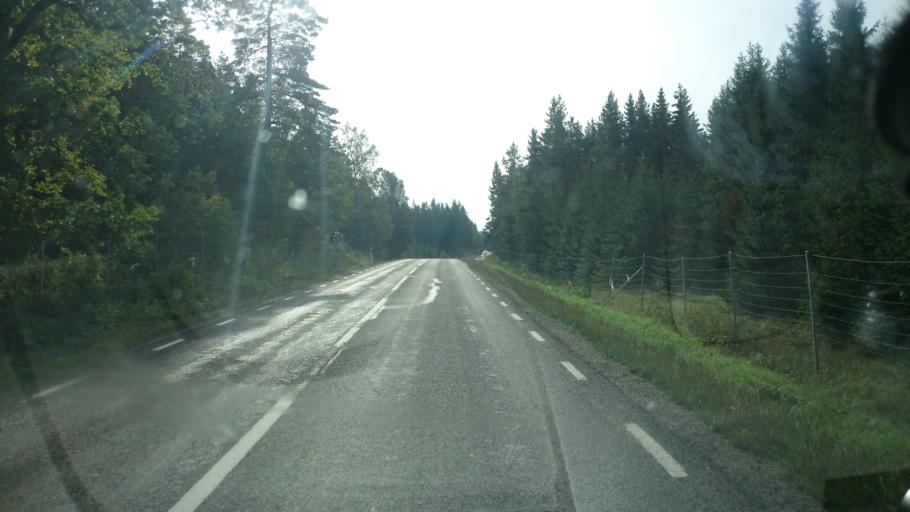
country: SE
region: Vaestra Goetaland
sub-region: Alingsas Kommun
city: Sollebrunn
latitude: 58.1465
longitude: 12.4182
